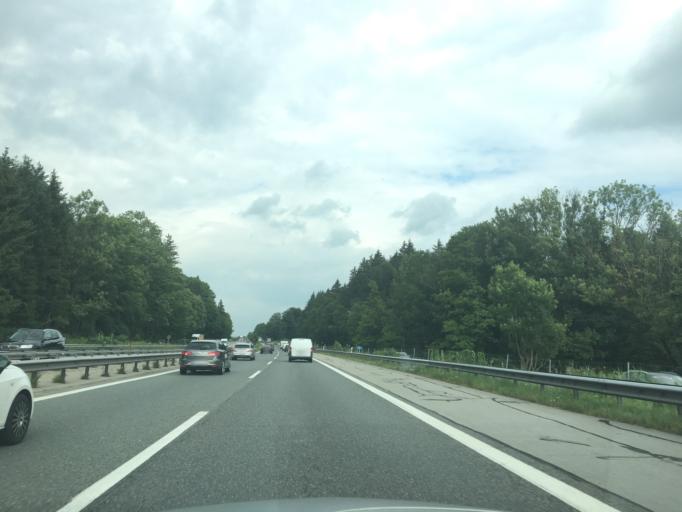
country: DE
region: Bavaria
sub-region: Upper Bavaria
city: Frasdorf
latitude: 47.7980
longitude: 12.2474
